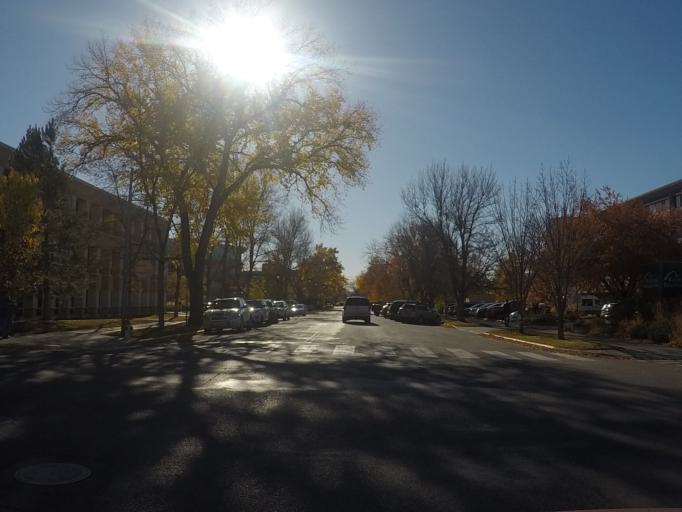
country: US
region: Montana
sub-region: Yellowstone County
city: Billings
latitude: 45.7884
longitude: -108.5138
